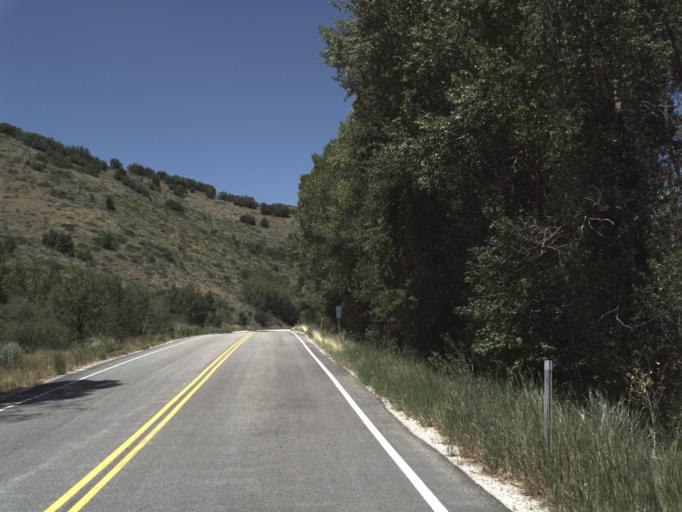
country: US
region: Utah
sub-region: Weber County
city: Wolf Creek
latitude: 41.3500
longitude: -111.5956
